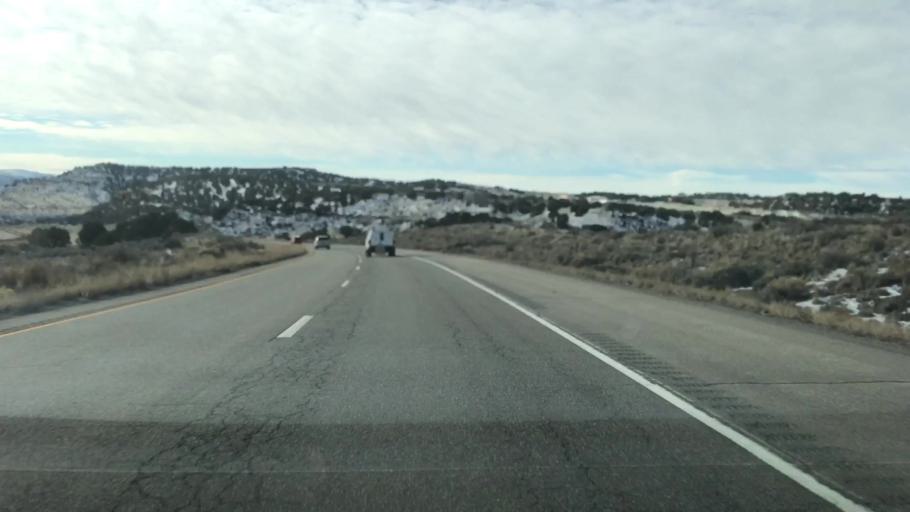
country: US
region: Colorado
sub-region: Garfield County
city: Parachute
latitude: 39.3719
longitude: -108.1679
